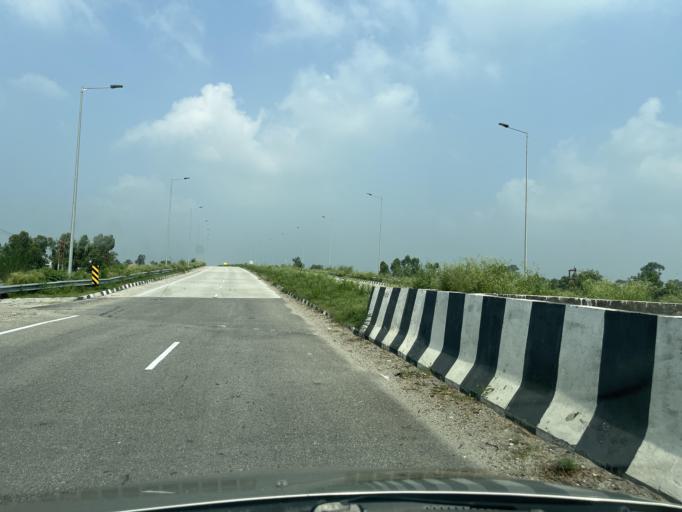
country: IN
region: Uttarakhand
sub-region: Udham Singh Nagar
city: Kashipur
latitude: 29.1712
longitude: 78.9509
